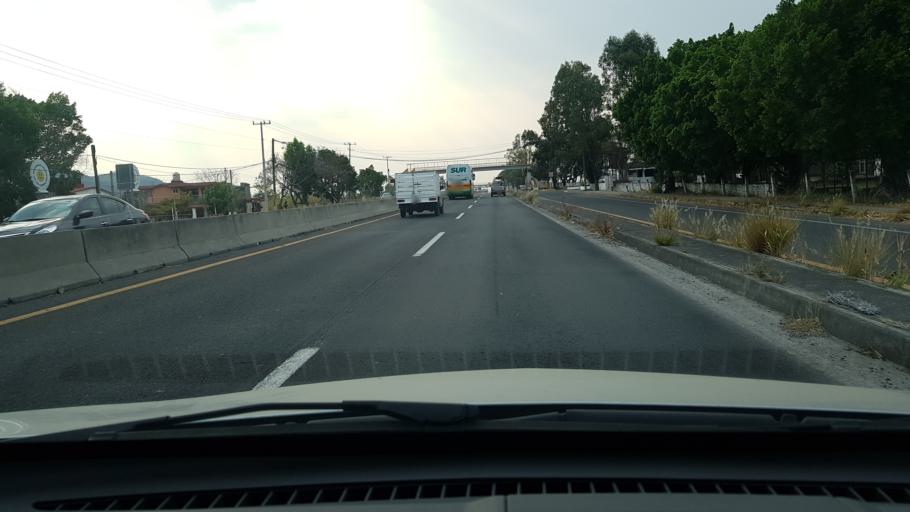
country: MX
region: Morelos
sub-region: Ayala
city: Unidad Habitacional Mariano Matamoros
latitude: 18.7478
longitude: -98.8455
